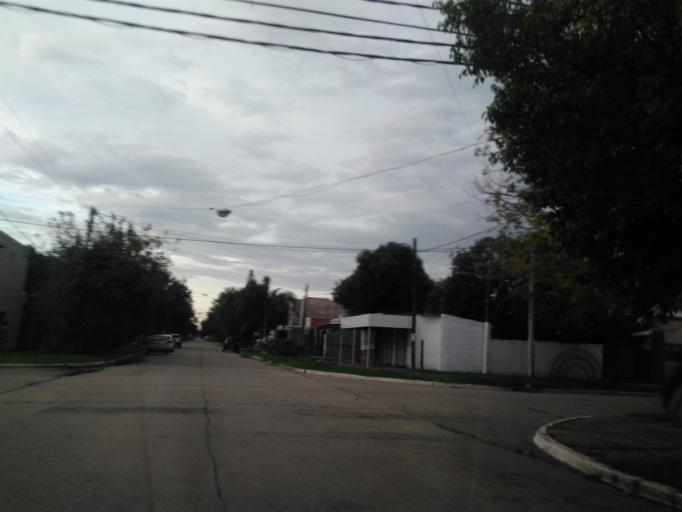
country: AR
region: Chaco
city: Resistencia
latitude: -27.4449
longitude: -58.9743
